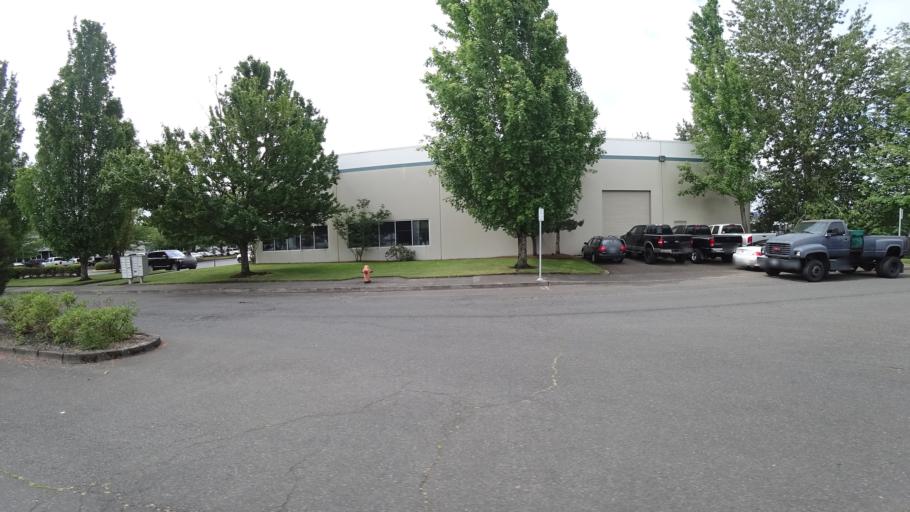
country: US
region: Washington
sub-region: Clark County
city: Vancouver
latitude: 45.6170
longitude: -122.6932
